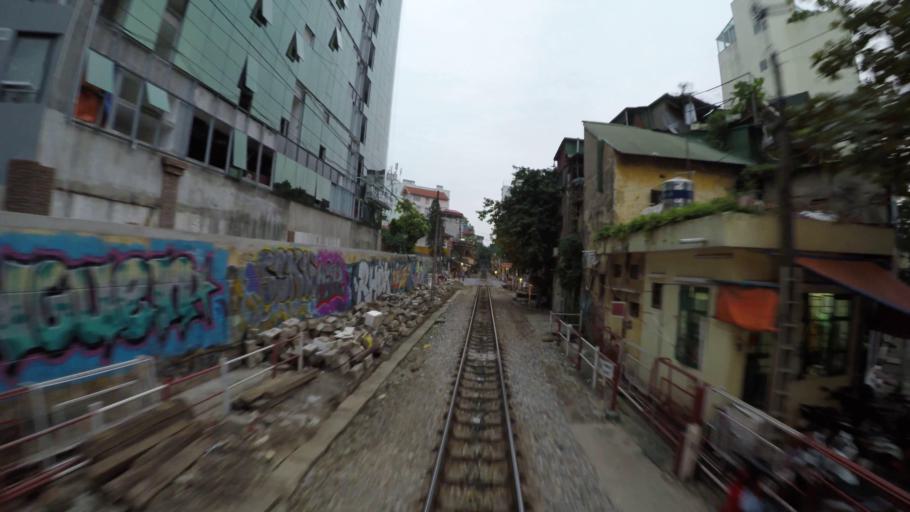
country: VN
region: Ha Noi
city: Hoan Kiem
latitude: 21.0361
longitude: 105.8459
